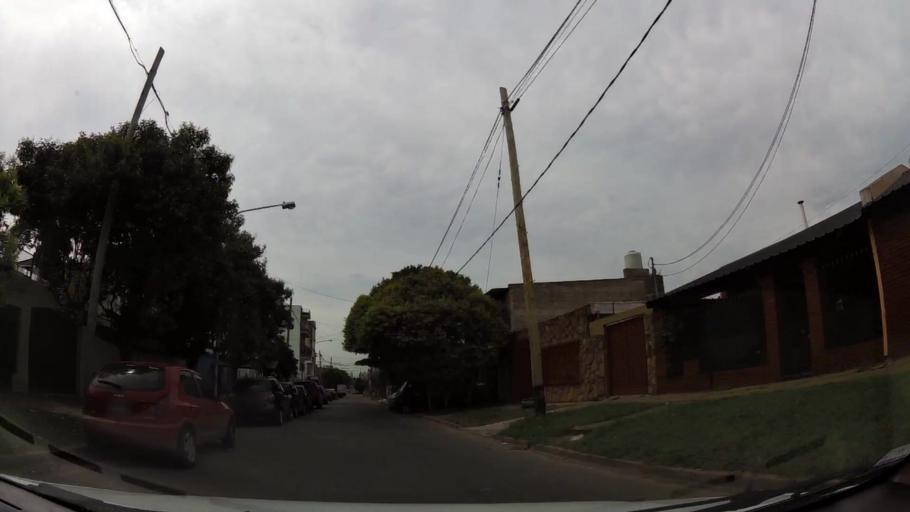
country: AR
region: Buenos Aires F.D.
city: Villa Lugano
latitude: -34.6976
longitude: -58.5152
